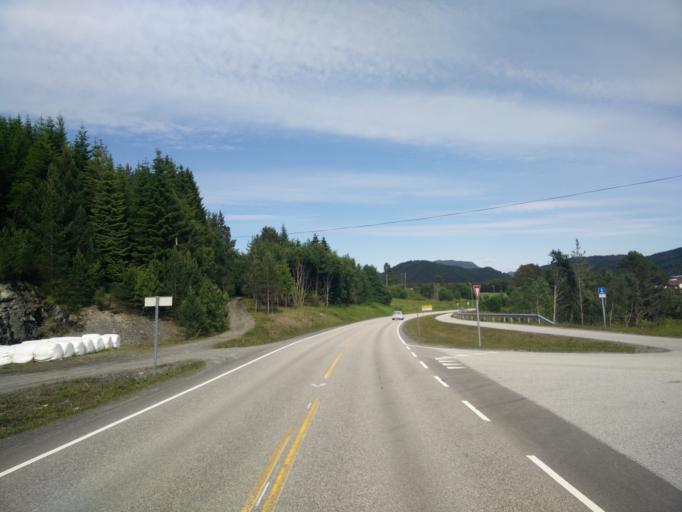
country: NO
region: More og Romsdal
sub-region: Kristiansund
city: Rensvik
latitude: 63.0091
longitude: 7.9641
